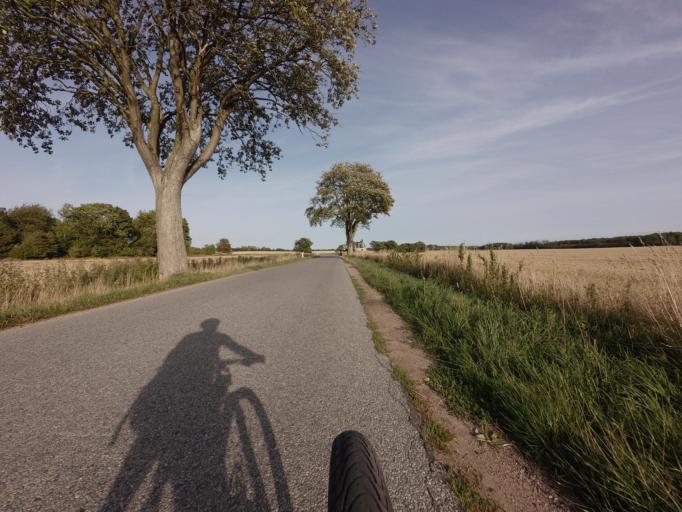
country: DK
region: Zealand
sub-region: Faxe Kommune
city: Fakse Ladeplads
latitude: 55.2501
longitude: 12.2301
